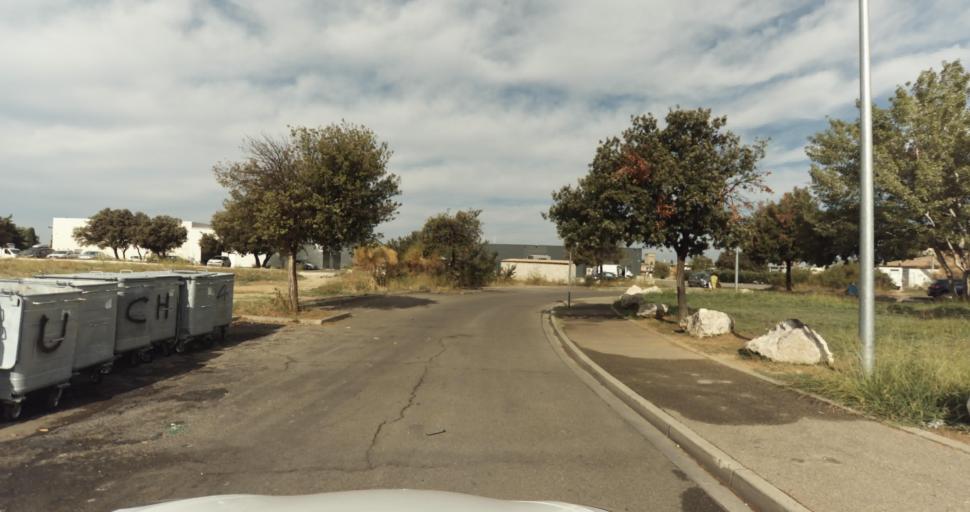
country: FR
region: Provence-Alpes-Cote d'Azur
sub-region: Departement des Bouches-du-Rhone
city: Miramas
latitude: 43.5991
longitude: 5.0076
